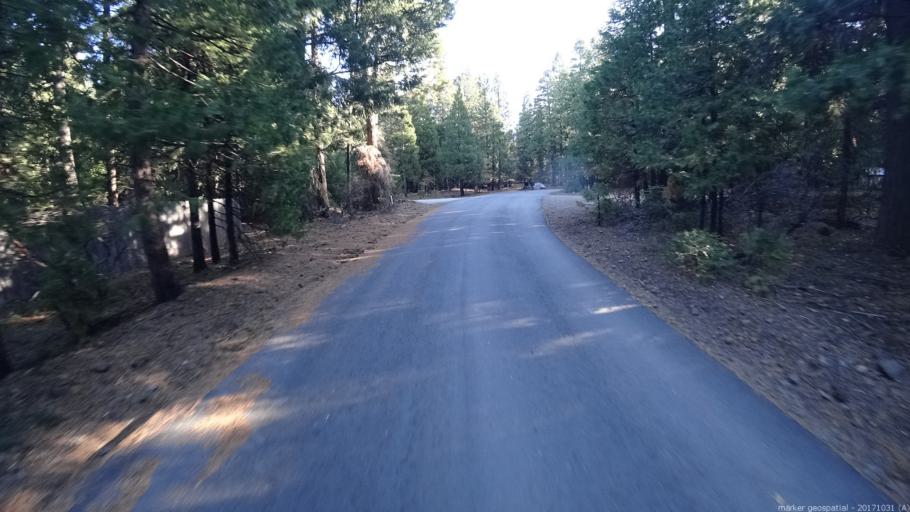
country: US
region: California
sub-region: Shasta County
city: Shingletown
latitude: 40.5271
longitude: -121.7589
